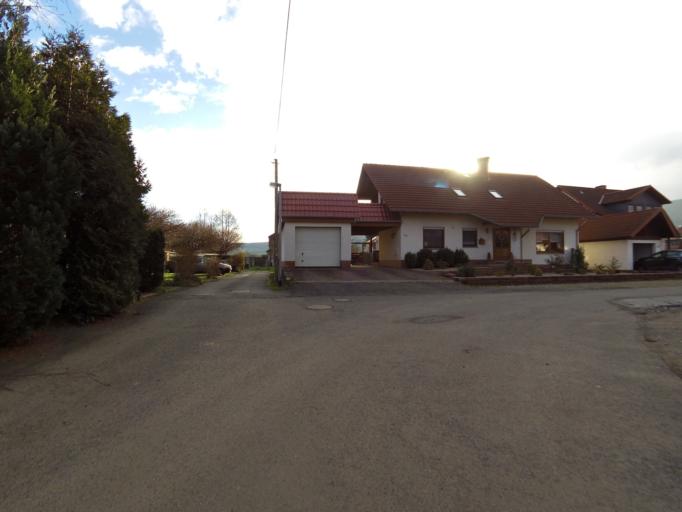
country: DE
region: Lower Saxony
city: Buhren
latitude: 51.4883
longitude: 9.6046
